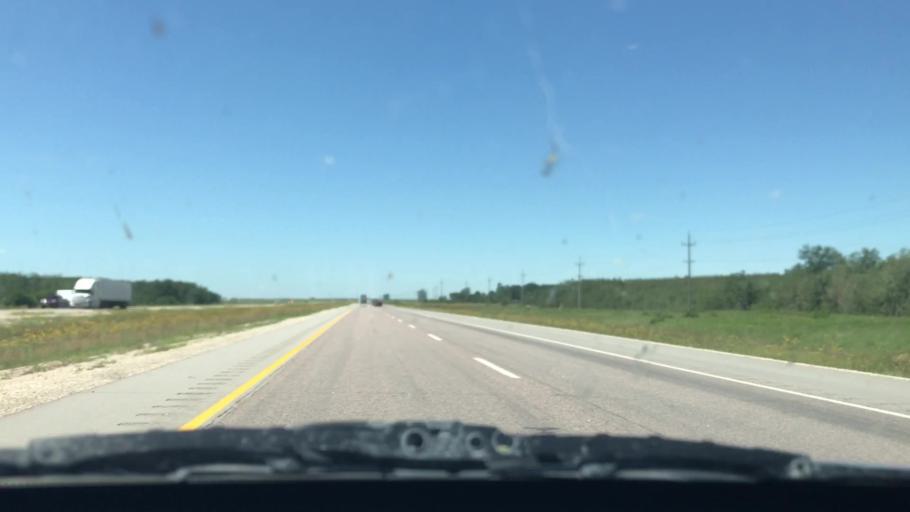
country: CA
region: Manitoba
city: Steinbach
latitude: 49.6855
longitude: -96.6066
